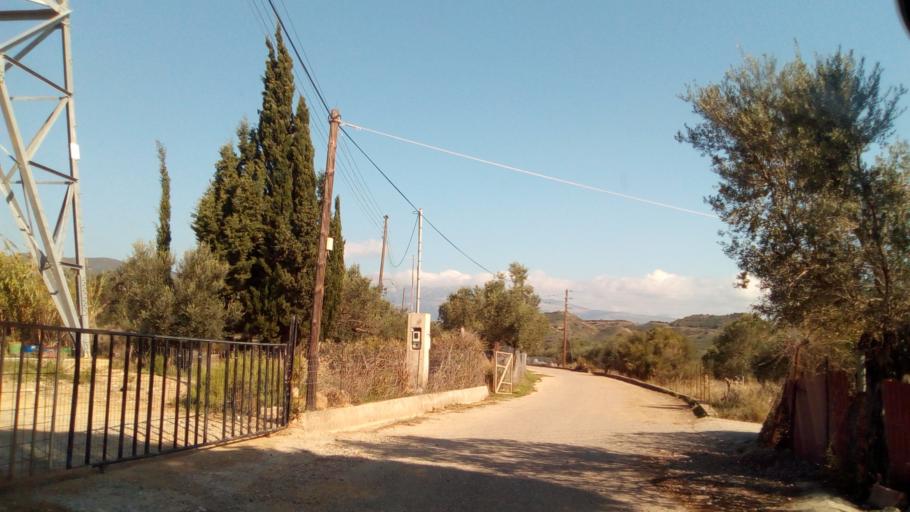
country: GR
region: West Greece
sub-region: Nomos Aitolias kai Akarnanias
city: Antirrio
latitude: 38.3451
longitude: 21.7612
